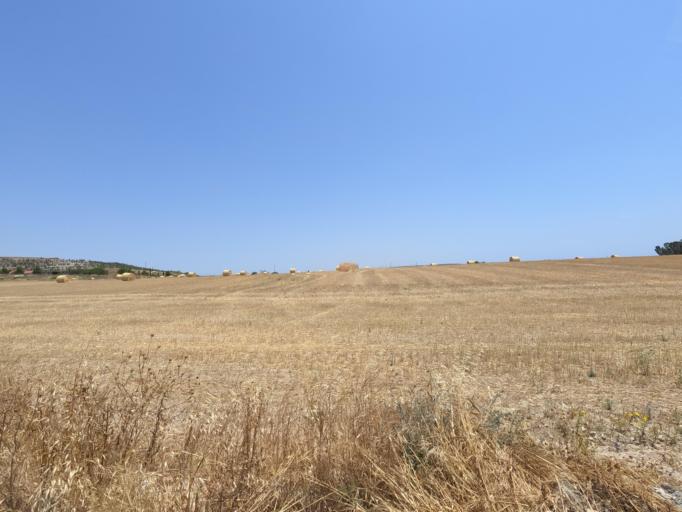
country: CY
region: Larnaka
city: Voroklini
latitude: 34.9960
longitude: 33.6668
